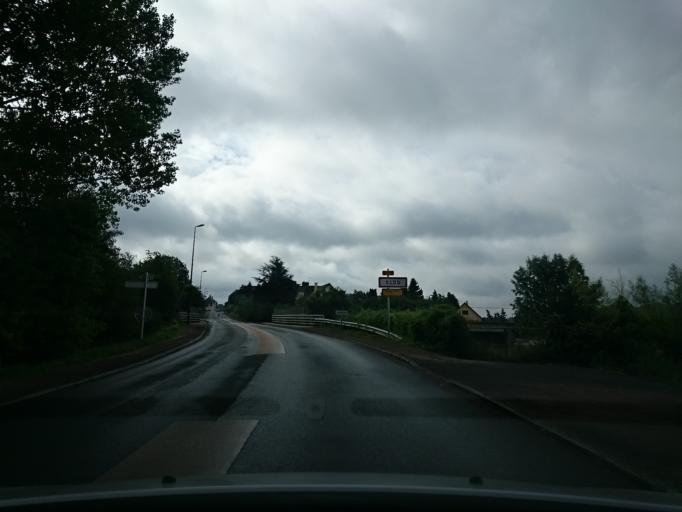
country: FR
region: Lower Normandy
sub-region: Departement du Calvados
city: Beuvillers
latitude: 49.1263
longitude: 0.2744
